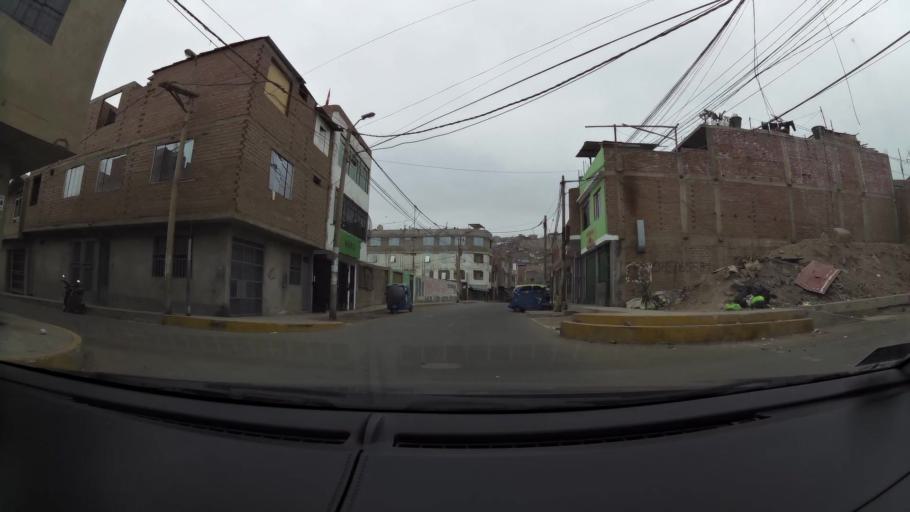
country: PE
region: Lima
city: Ventanilla
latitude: -11.9349
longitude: -77.0874
